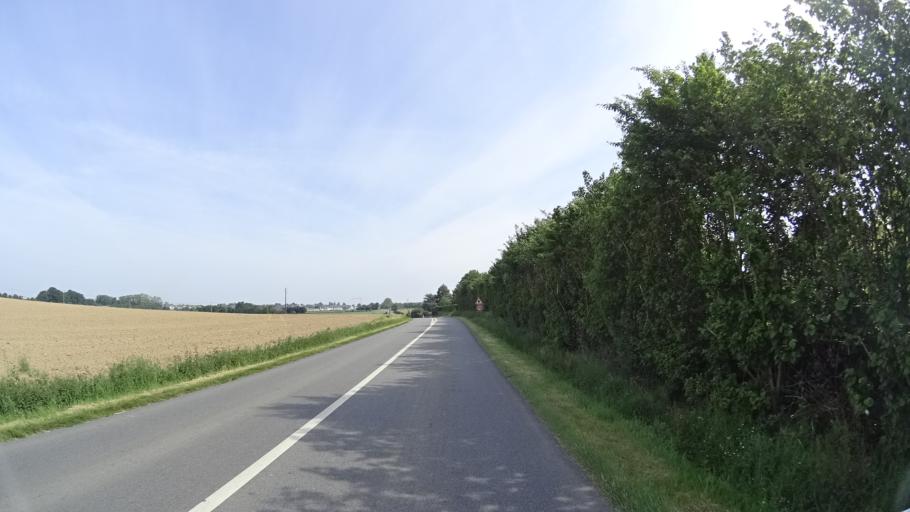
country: FR
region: Brittany
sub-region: Departement d'Ille-et-Vilaine
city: Chateaugiron
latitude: 48.0315
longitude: -1.5044
